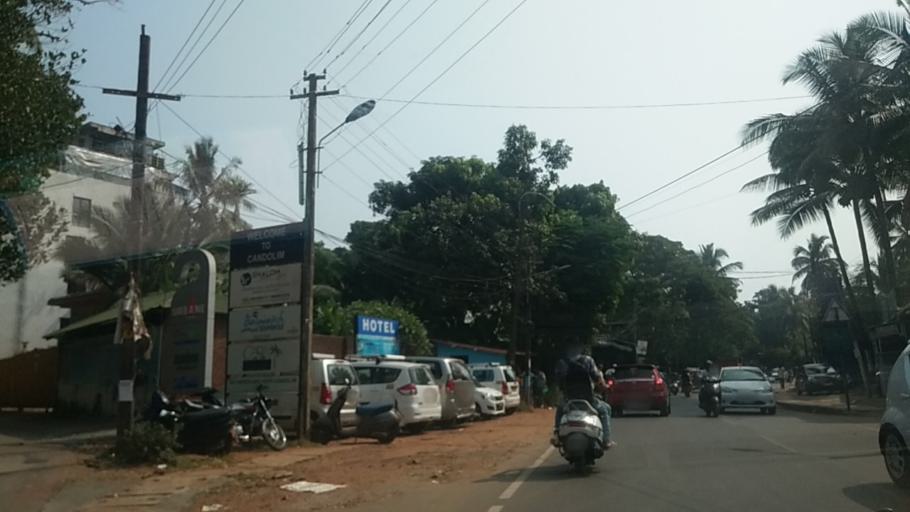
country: IN
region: Goa
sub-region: North Goa
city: Candolim
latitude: 15.5297
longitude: 73.7648
